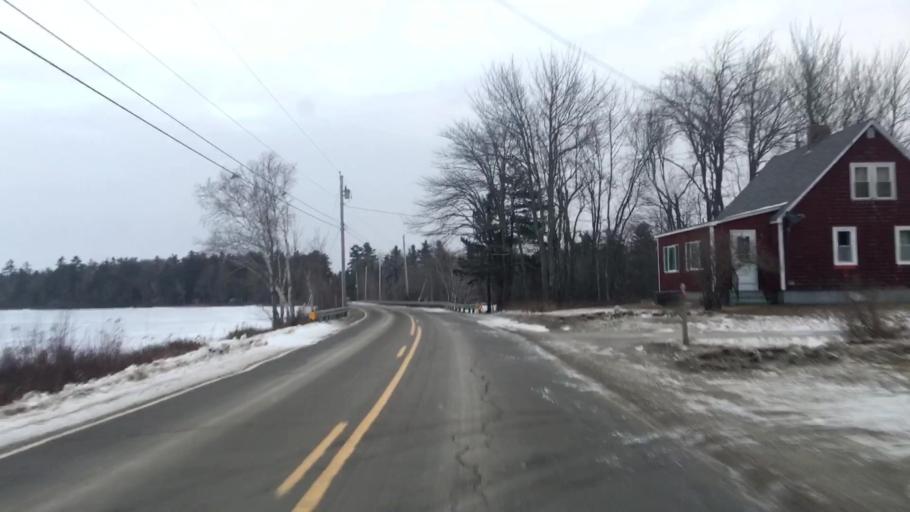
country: US
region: Maine
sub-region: Hancock County
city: Ellsworth
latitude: 44.6127
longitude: -68.3876
